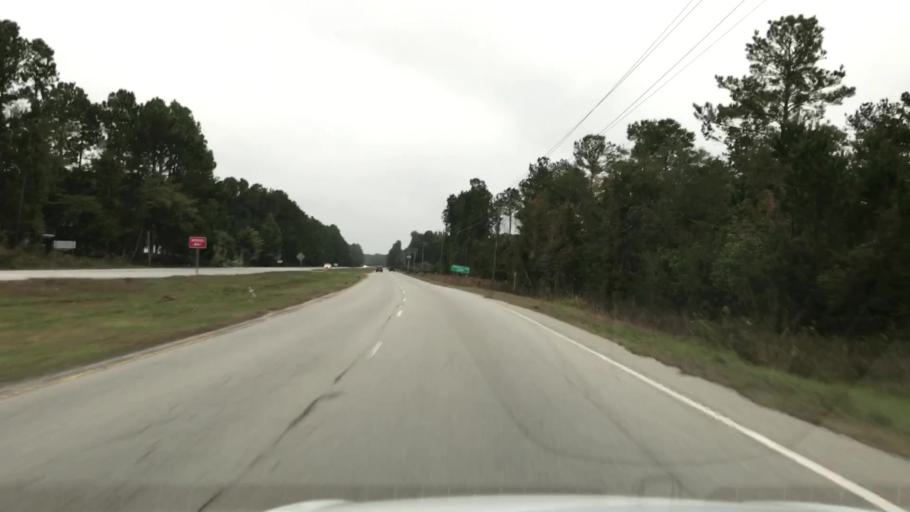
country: US
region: South Carolina
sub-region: Charleston County
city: Awendaw
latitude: 32.9907
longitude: -79.6458
